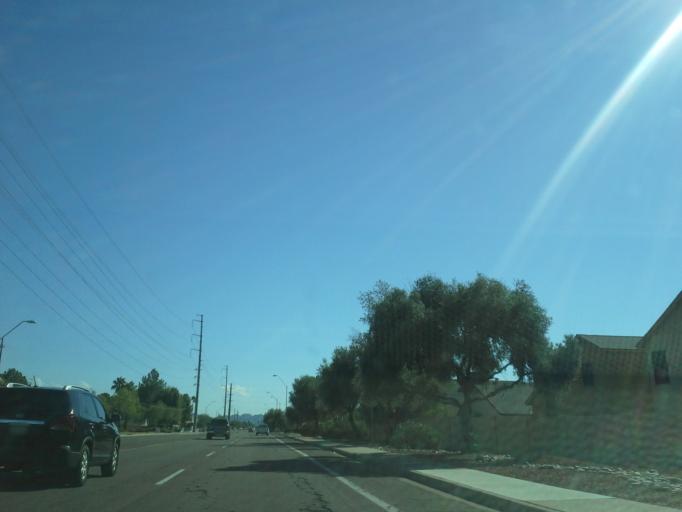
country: US
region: Arizona
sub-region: Maricopa County
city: Paradise Valley
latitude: 33.6607
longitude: -112.0137
